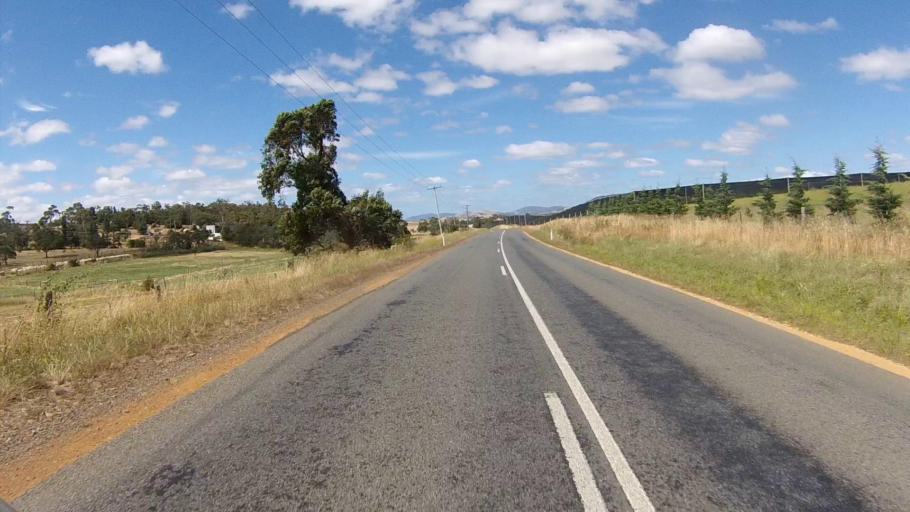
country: AU
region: Tasmania
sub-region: Sorell
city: Sorell
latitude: -42.6450
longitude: 147.4340
